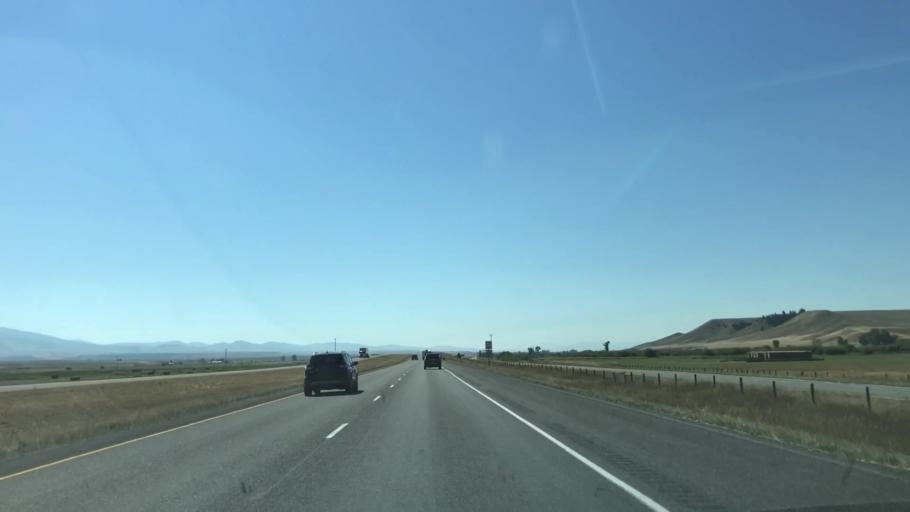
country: US
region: Montana
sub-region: Powell County
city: Deer Lodge
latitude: 46.4814
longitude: -112.7235
